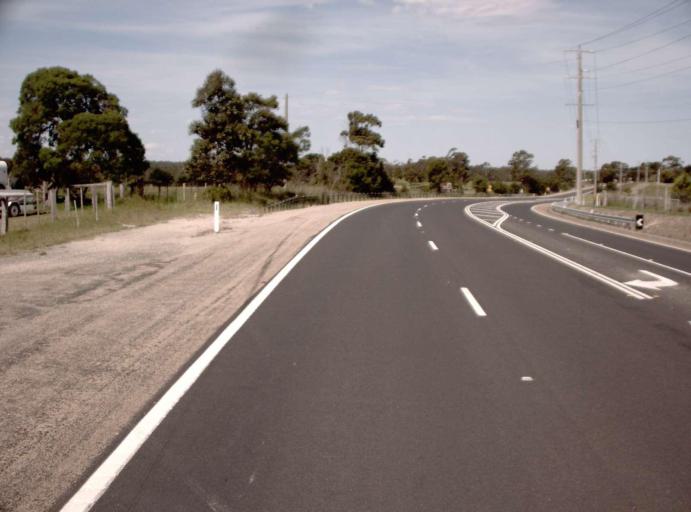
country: AU
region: Victoria
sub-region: East Gippsland
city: Lakes Entrance
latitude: -37.8515
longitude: 147.9371
